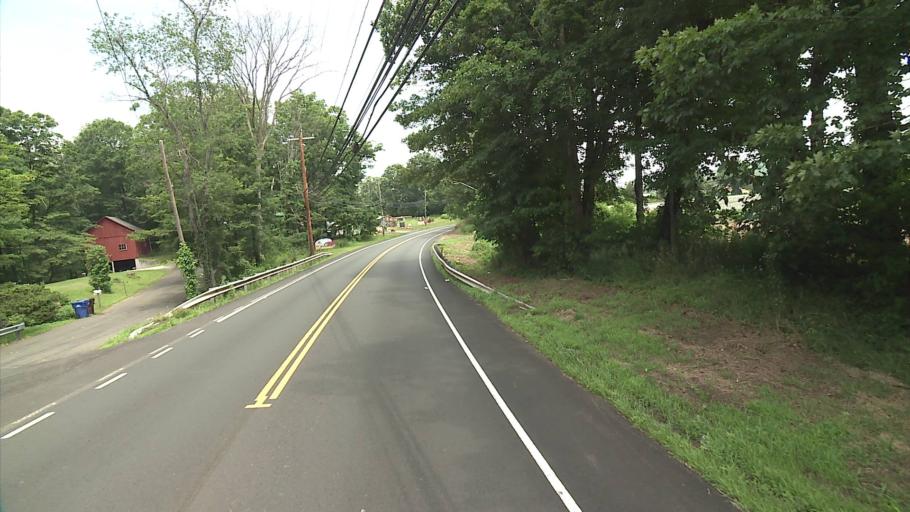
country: US
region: Connecticut
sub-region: New Haven County
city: North Branford
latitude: 41.3565
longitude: -72.8028
